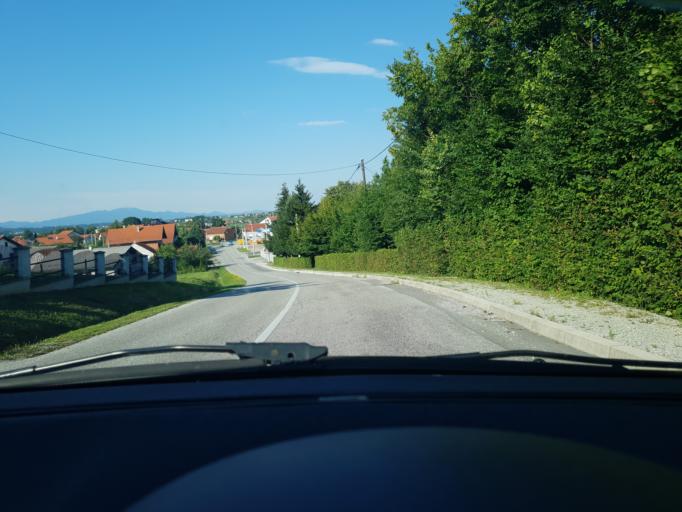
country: HR
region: Krapinsko-Zagorska
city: Oroslavje
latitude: 45.9871
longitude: 15.9152
